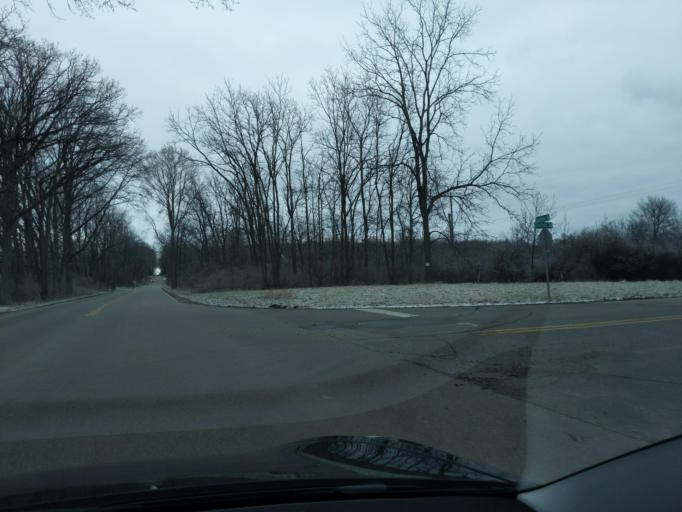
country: US
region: Michigan
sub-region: Jackson County
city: Spring Arbor
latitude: 42.2402
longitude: -84.5176
